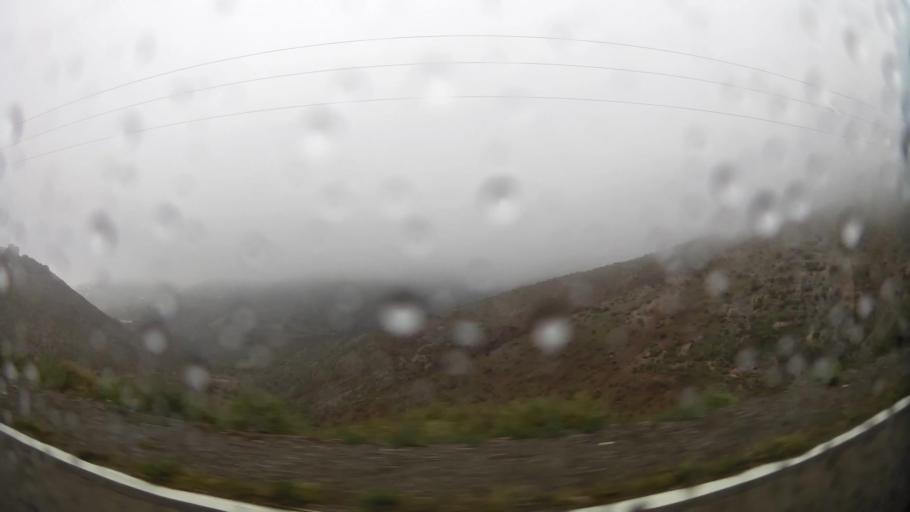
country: MA
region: Taza-Al Hoceima-Taounate
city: Tirhanimine
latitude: 35.2356
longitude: -3.9709
